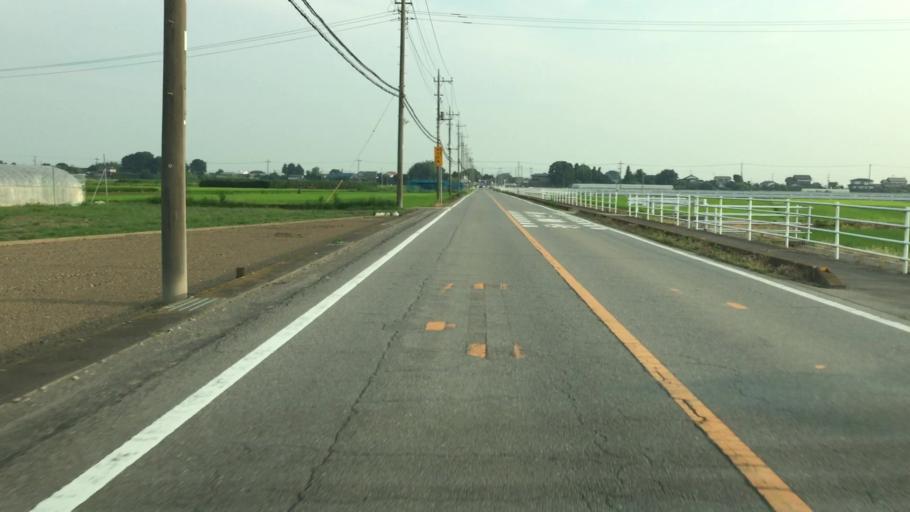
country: JP
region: Tochigi
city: Fujioka
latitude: 36.2563
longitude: 139.6211
